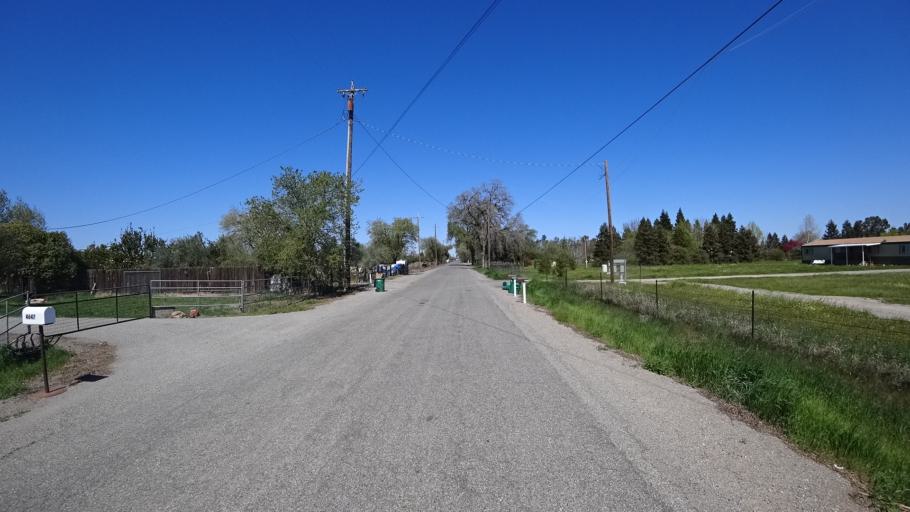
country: US
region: California
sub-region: Glenn County
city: Orland
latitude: 39.7676
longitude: -122.2296
